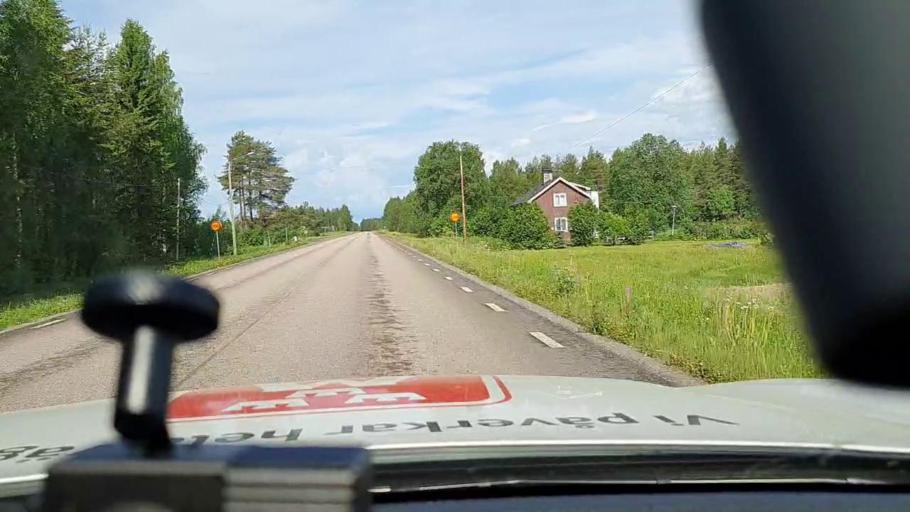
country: SE
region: Norrbotten
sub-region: Alvsbyns Kommun
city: AElvsbyn
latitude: 66.0177
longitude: 21.1502
